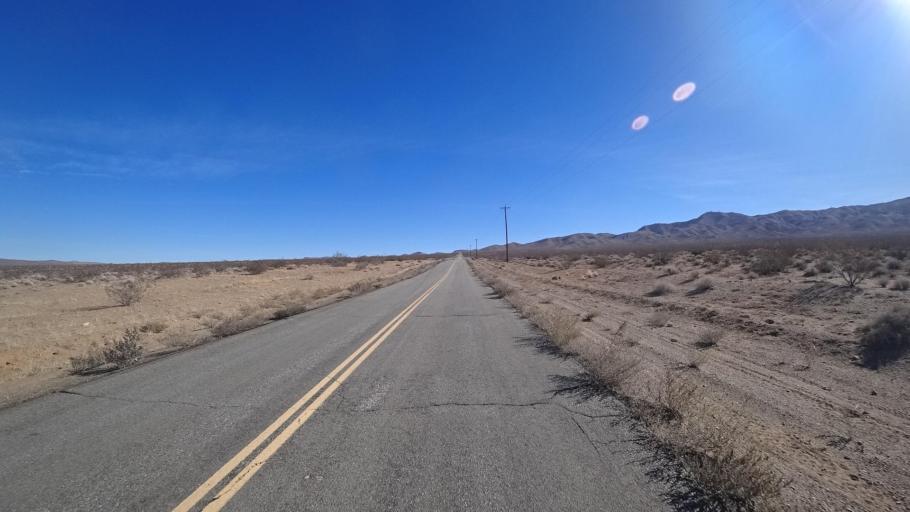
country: US
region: California
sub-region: Kern County
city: Ridgecrest
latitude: 35.3840
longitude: -117.7135
